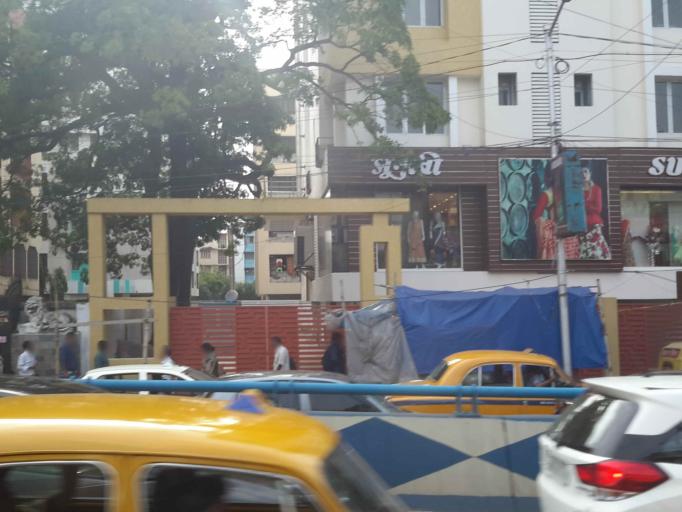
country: IN
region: West Bengal
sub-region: Kolkata
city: Kolkata
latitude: 22.5221
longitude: 88.3651
